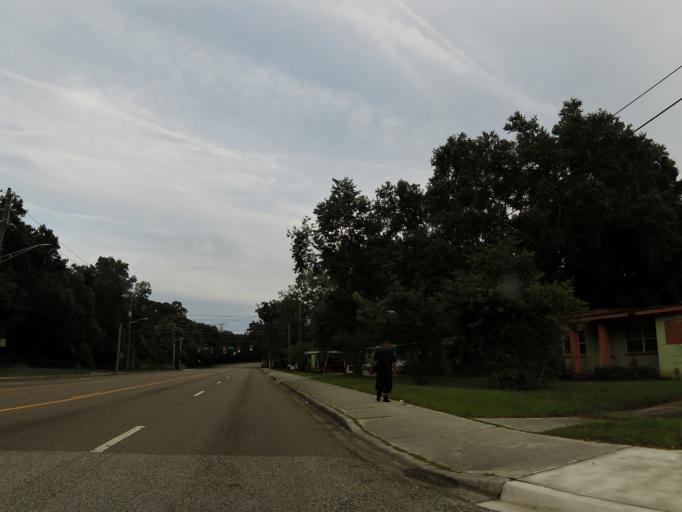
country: US
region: Florida
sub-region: Duval County
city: Jacksonville
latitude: 30.3825
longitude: -81.7006
